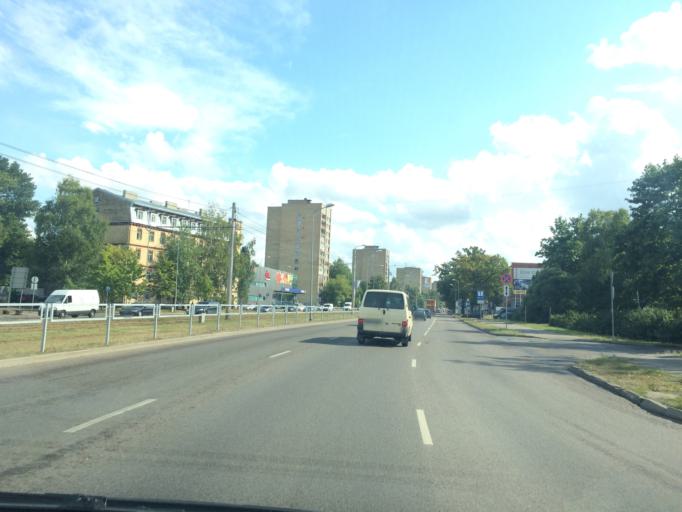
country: LV
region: Kekava
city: Balozi
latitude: 56.9215
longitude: 24.1705
